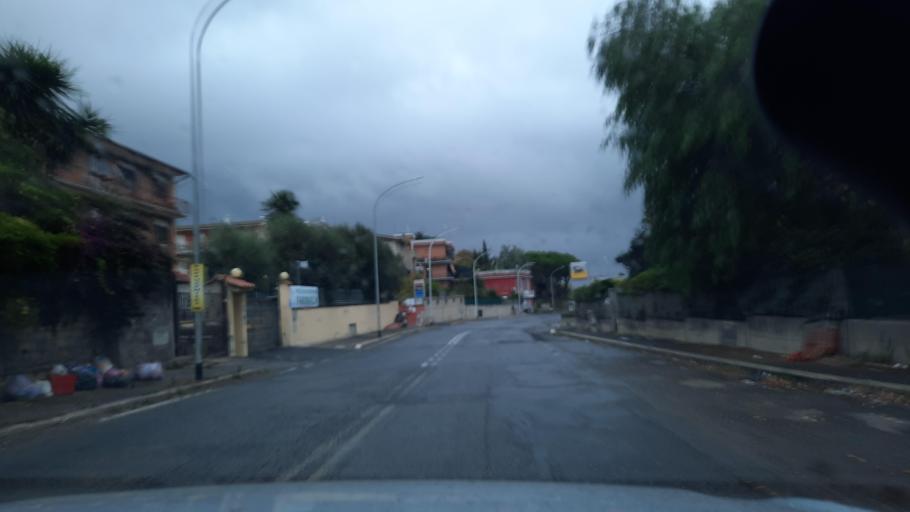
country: IT
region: Latium
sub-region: Citta metropolitana di Roma Capitale
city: Ponte Galeria-La Pisana
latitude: 41.8195
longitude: 12.3539
